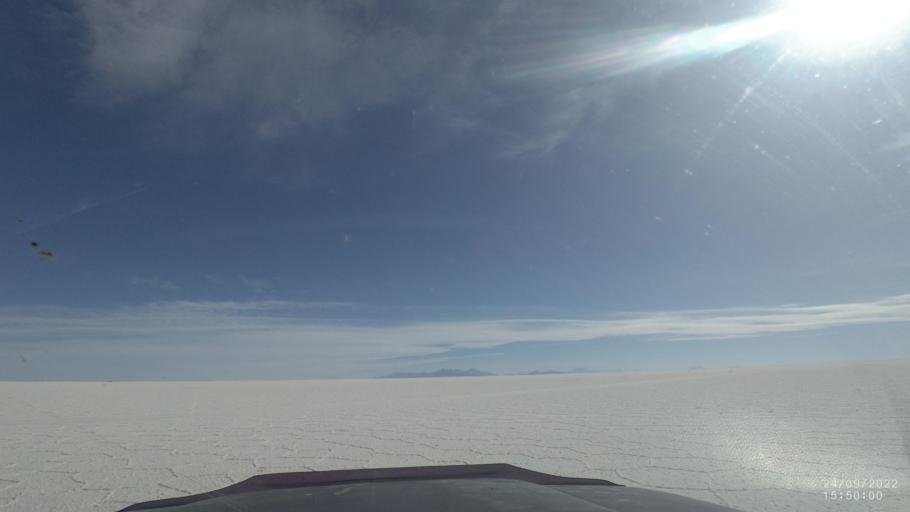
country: BO
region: Potosi
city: Colchani
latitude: -20.3056
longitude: -67.2464
